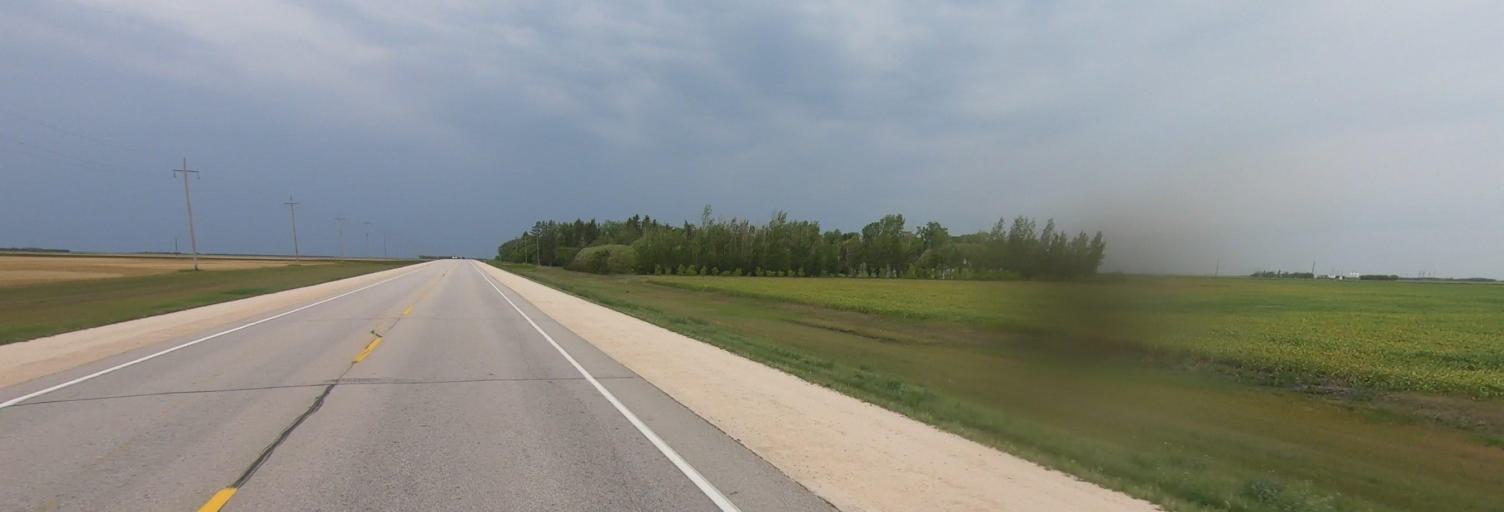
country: CA
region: Manitoba
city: Headingley
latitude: 49.7685
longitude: -97.3862
